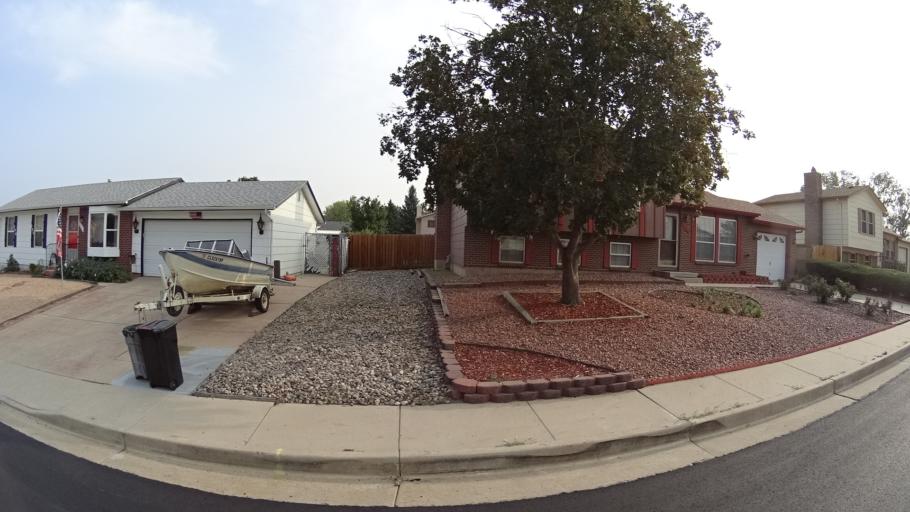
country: US
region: Colorado
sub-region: El Paso County
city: Stratmoor
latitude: 38.7984
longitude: -104.7545
